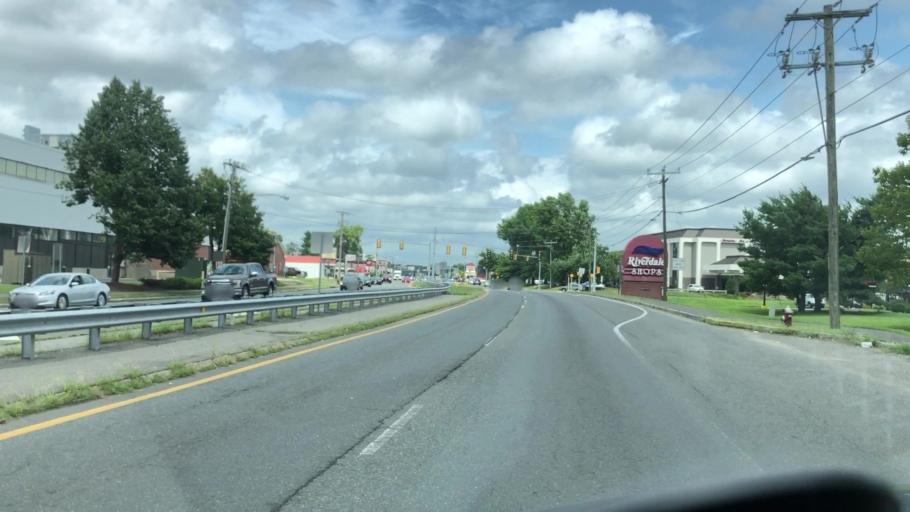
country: US
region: Massachusetts
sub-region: Hampden County
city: West Springfield
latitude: 42.1300
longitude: -72.6262
